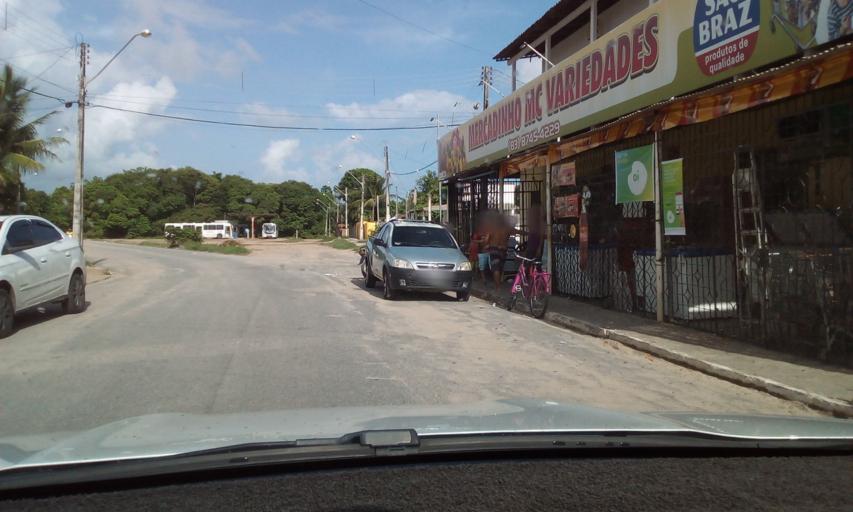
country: BR
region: Paraiba
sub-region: Joao Pessoa
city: Joao Pessoa
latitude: -7.1825
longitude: -34.8258
